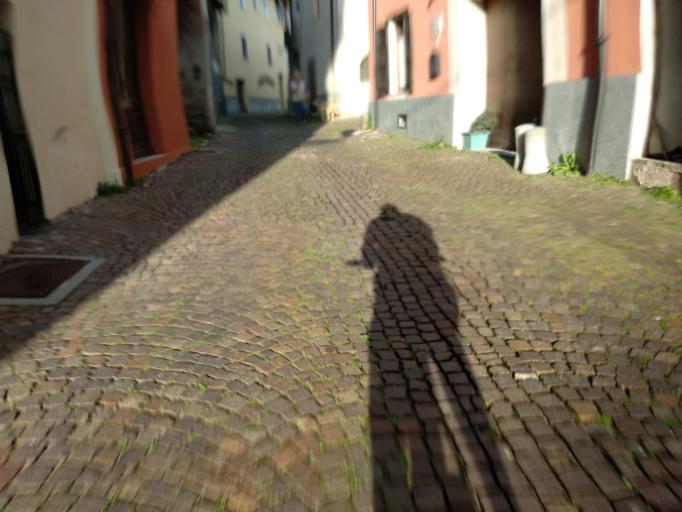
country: IT
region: Piedmont
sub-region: Provincia di Cuneo
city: Garessio
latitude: 44.1970
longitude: 8.0301
